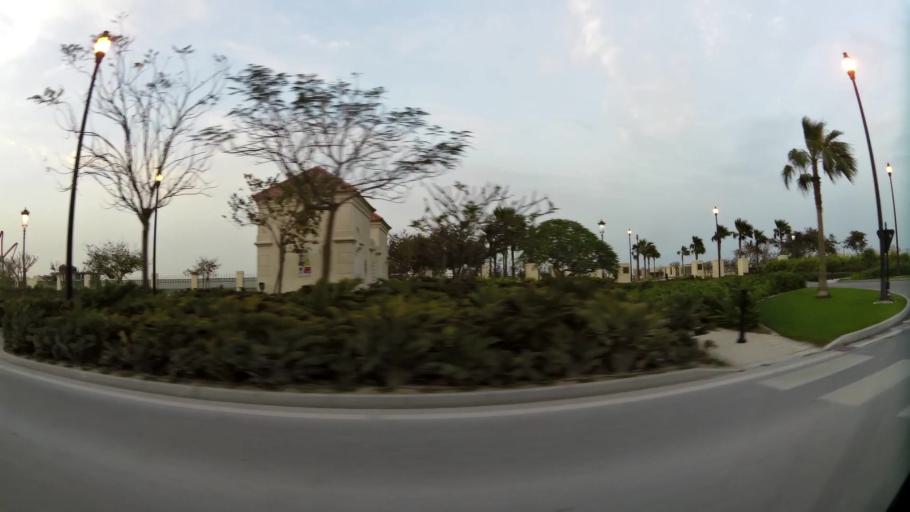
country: QA
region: Baladiyat ad Dawhah
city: Doha
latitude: 25.3596
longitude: 51.5682
